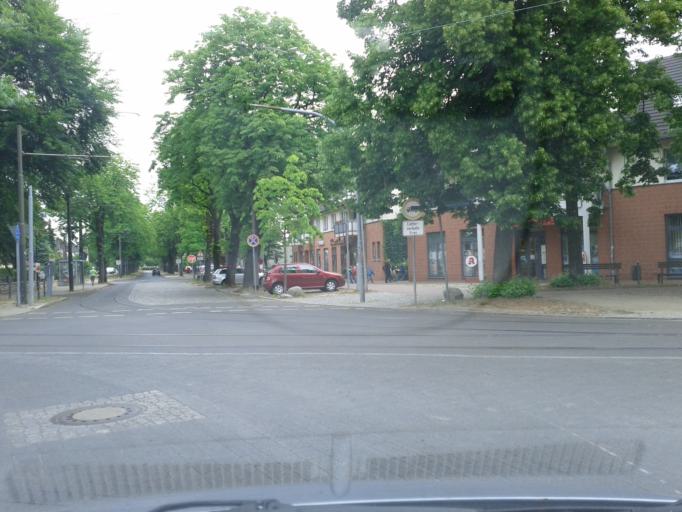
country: DE
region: Brandenburg
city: Woltersdorf
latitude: 52.4503
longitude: 13.7533
